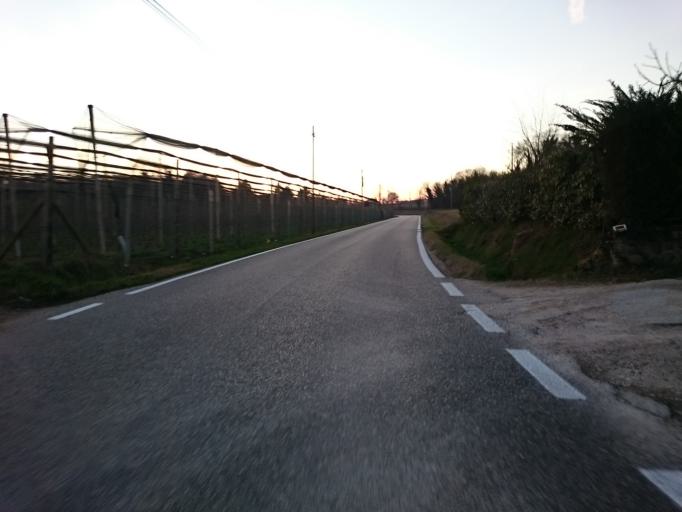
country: IT
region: Veneto
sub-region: Provincia di Verona
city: Salionze
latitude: 45.4074
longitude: 10.7394
